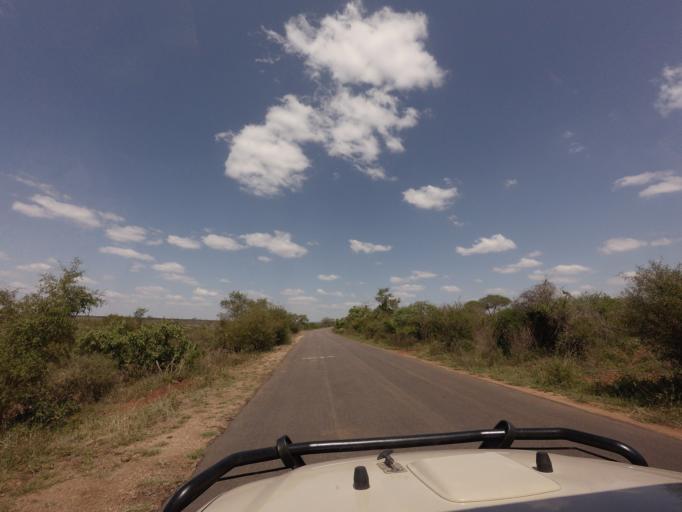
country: ZA
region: Mpumalanga
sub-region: Ehlanzeni District
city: Komatipoort
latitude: -25.1021
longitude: 31.8937
